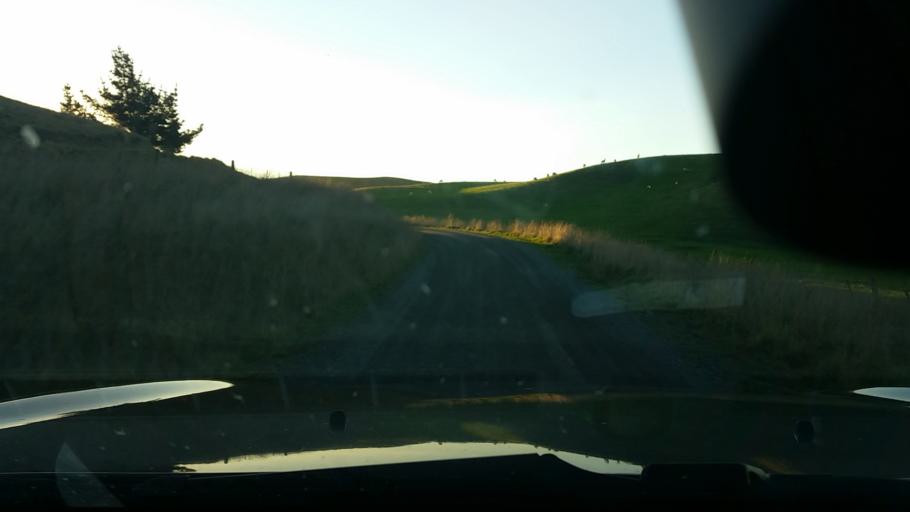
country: NZ
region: Marlborough
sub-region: Marlborough District
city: Blenheim
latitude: -41.7435
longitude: 174.0556
